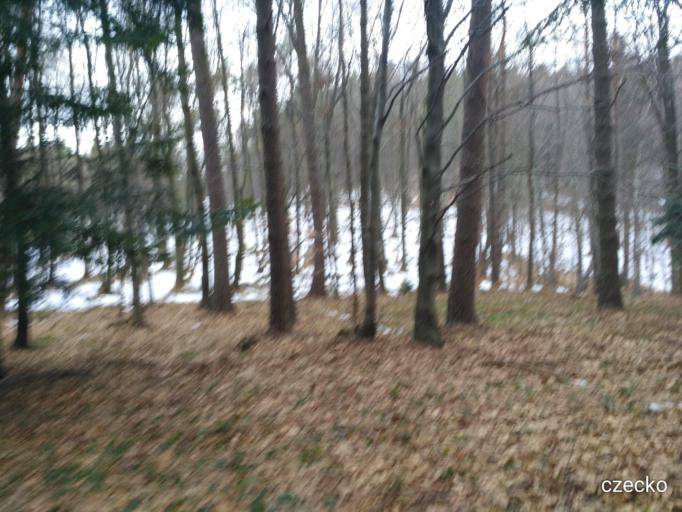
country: PL
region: Subcarpathian Voivodeship
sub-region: Powiat krosnienski
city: Korczyna
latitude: 49.7517
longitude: 21.8263
